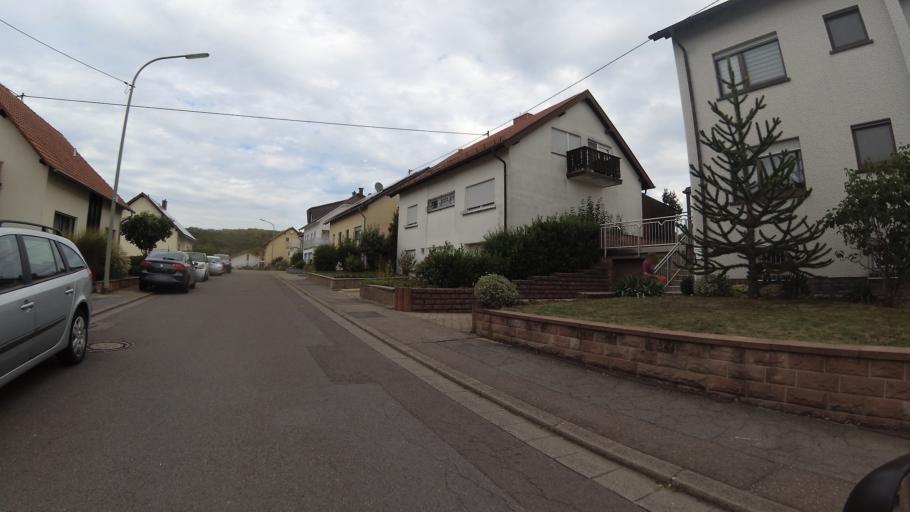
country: DE
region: Saarland
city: Kleinblittersdorf
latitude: 49.1472
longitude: 7.0520
